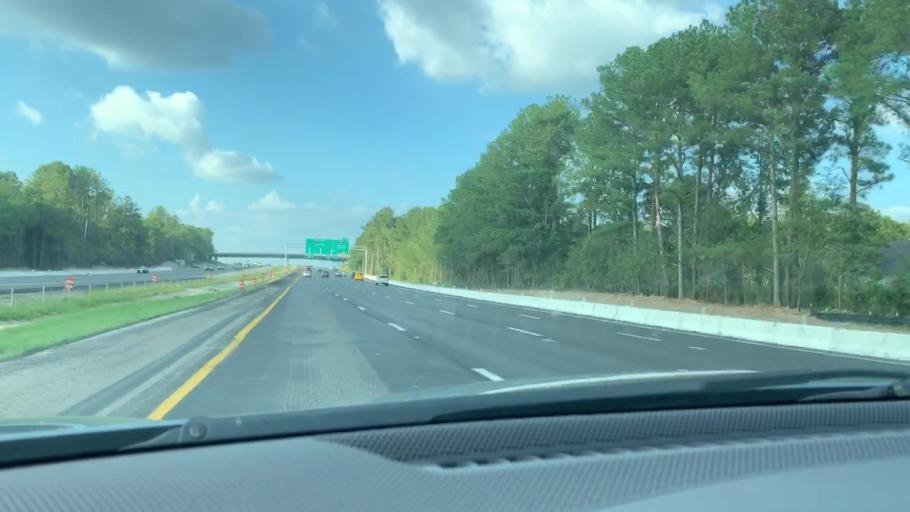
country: US
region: South Carolina
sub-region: Richland County
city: Woodfield
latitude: 34.0587
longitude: -80.9223
